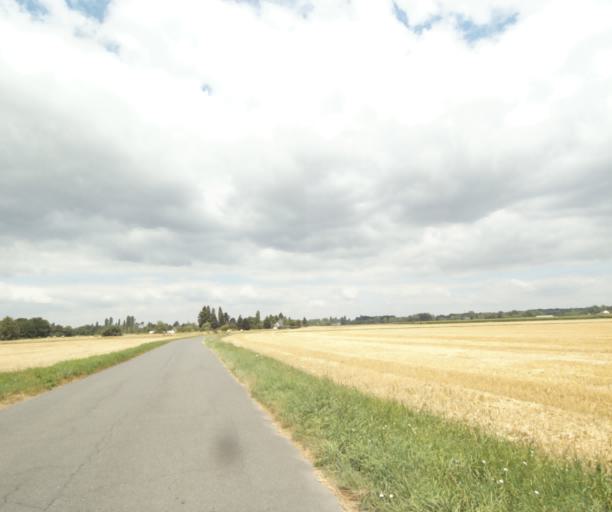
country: FR
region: Centre
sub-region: Departement du Loiret
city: Mardie
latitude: 47.8795
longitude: 2.0398
